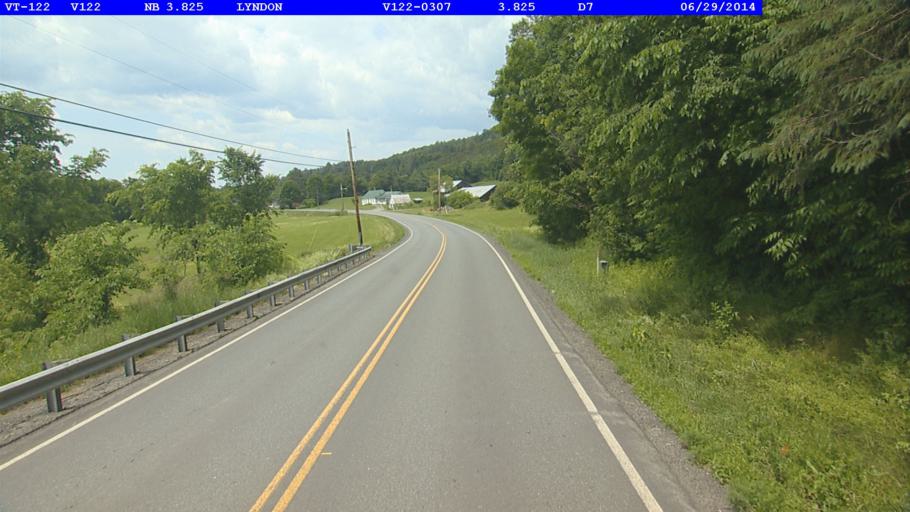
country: US
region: Vermont
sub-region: Caledonia County
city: Lyndonville
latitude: 44.5756
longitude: -72.0542
